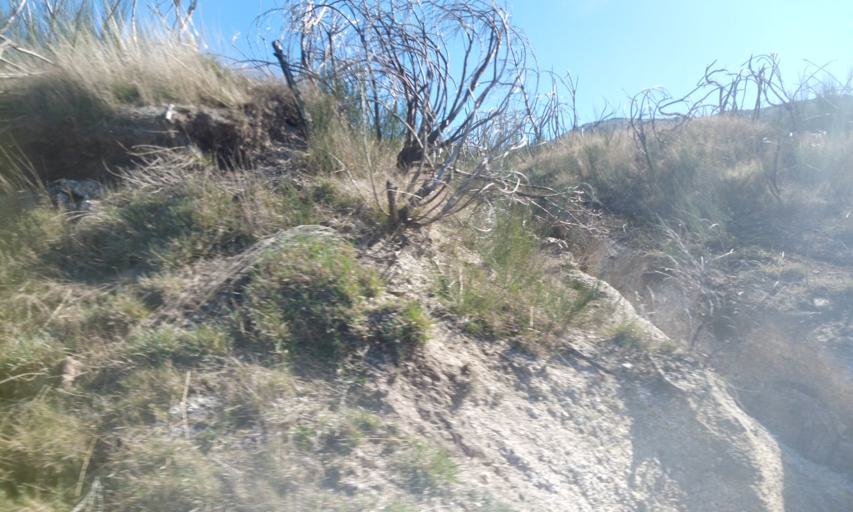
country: PT
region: Guarda
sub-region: Manteigas
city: Manteigas
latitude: 40.4887
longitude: -7.5512
